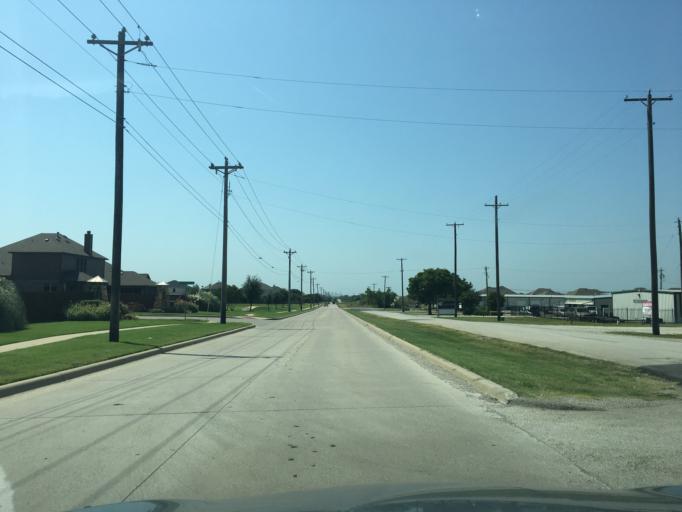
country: US
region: Texas
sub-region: Tarrant County
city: Haslet
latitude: 32.9215
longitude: -97.3315
